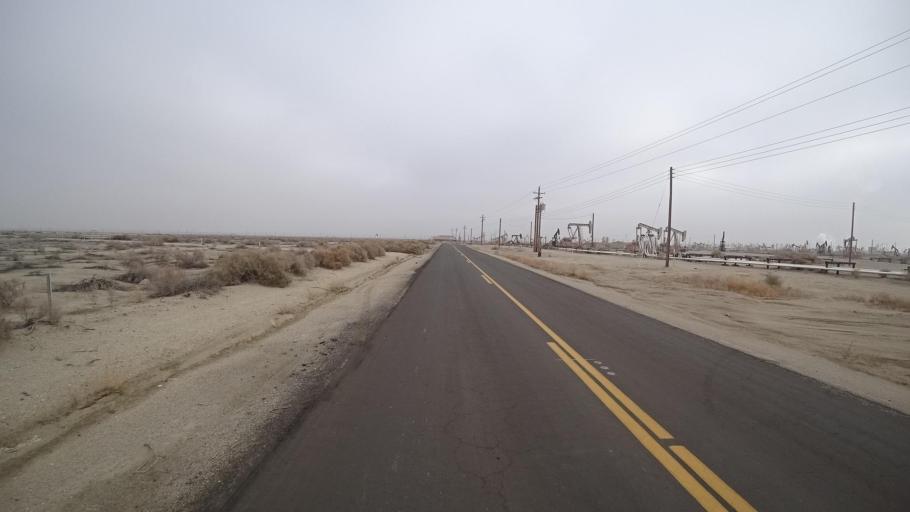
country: US
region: California
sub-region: Kern County
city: Maricopa
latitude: 35.0837
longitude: -119.3908
